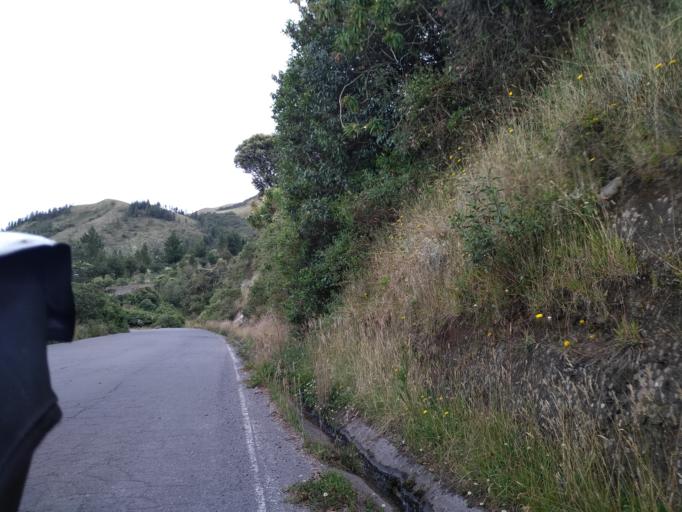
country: EC
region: Cotopaxi
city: Saquisili
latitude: -0.7140
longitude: -78.7637
